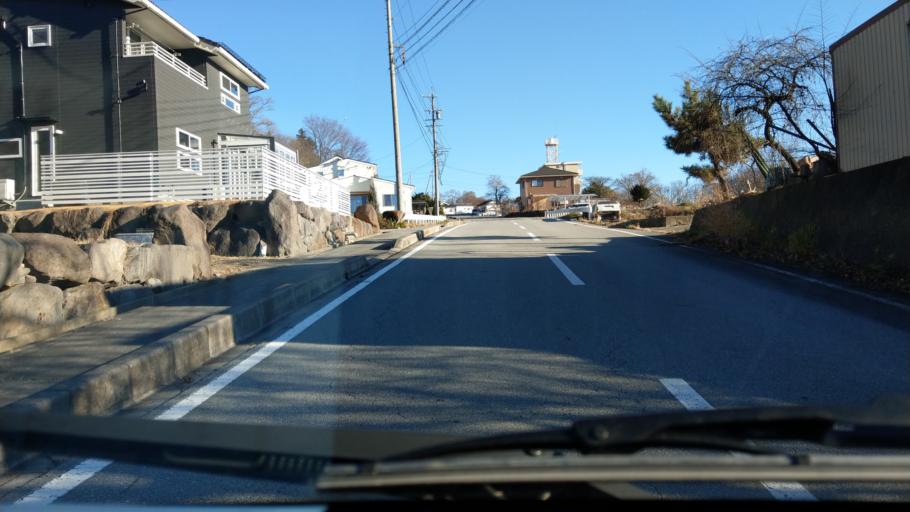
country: JP
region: Nagano
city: Komoro
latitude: 36.3210
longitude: 138.4239
